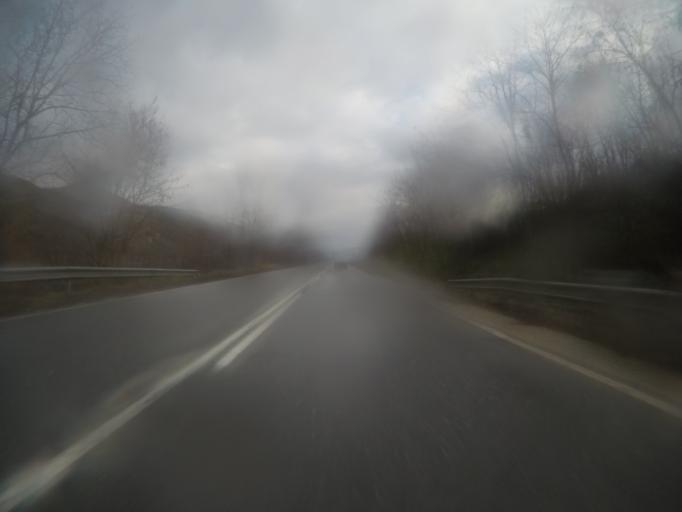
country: BG
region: Blagoevgrad
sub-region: Obshtina Simitli
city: Simitli
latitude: 41.8839
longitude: 23.1499
